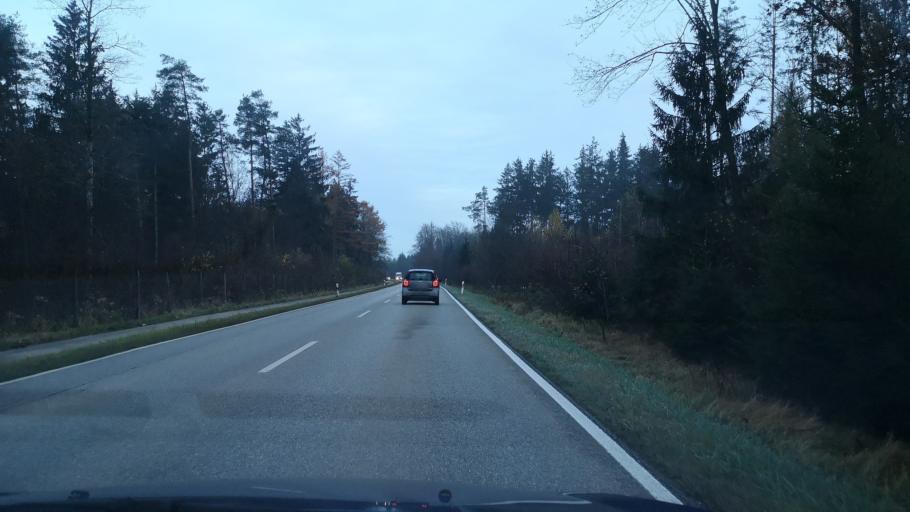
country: DE
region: Bavaria
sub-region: Upper Bavaria
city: Forstinning
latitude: 48.1501
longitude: 11.9149
